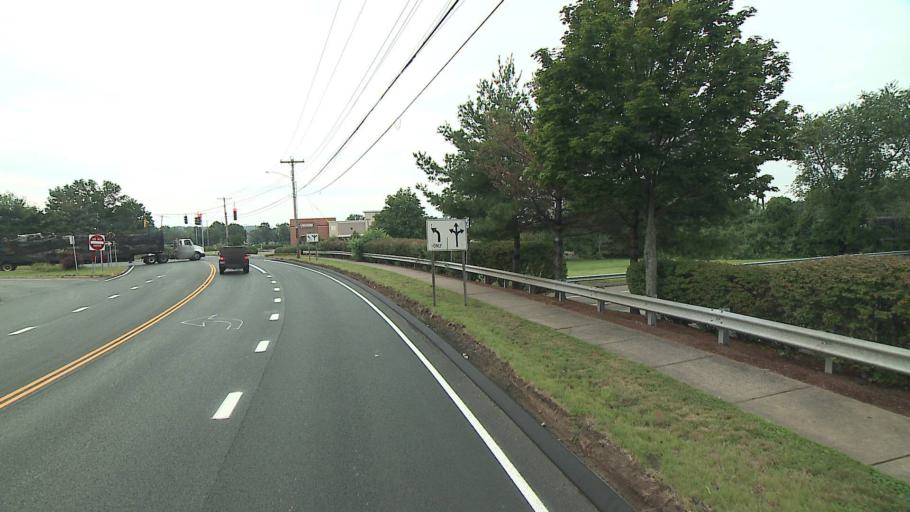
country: US
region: Connecticut
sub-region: New Haven County
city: North Haven
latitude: 41.3495
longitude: -72.8692
